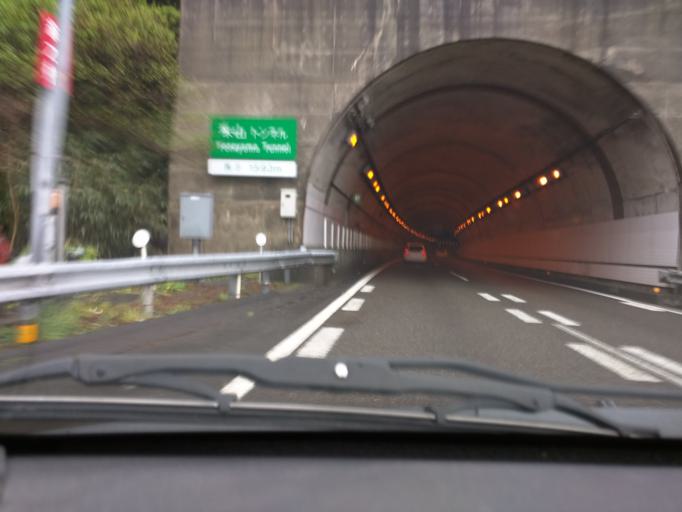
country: JP
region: Niigata
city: Kashiwazaki
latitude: 37.3209
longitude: 138.4567
